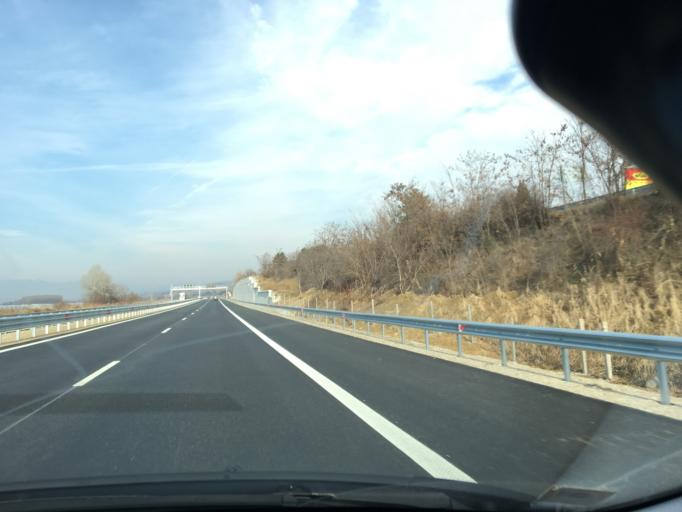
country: BG
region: Blagoevgrad
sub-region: Obshtina Sandanski
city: Sandanski
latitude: 41.5698
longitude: 23.2407
